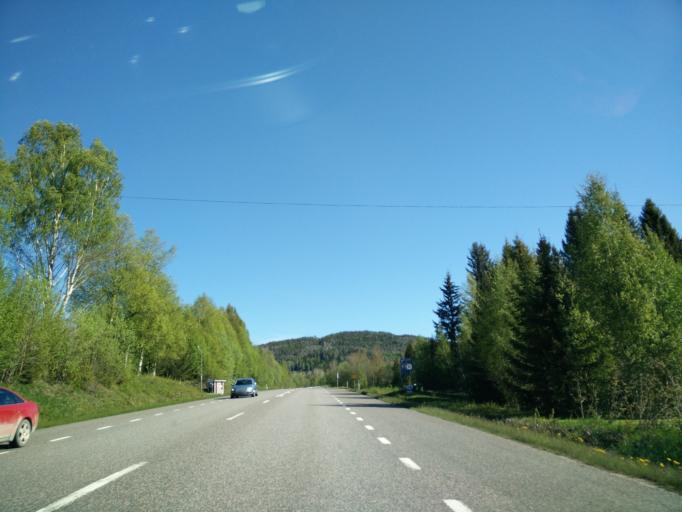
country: SE
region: Vaesternorrland
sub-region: Kramfors Kommun
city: Nordingra
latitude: 63.0214
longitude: 18.2965
